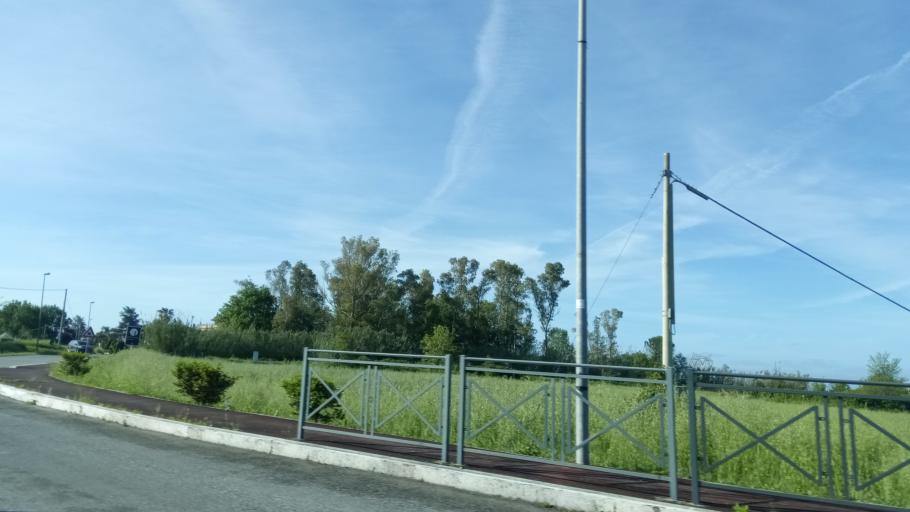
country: IT
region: Latium
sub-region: Provincia di Latina
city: Grunuovo-Campomaggiore San Luca
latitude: 41.2695
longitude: 13.7893
